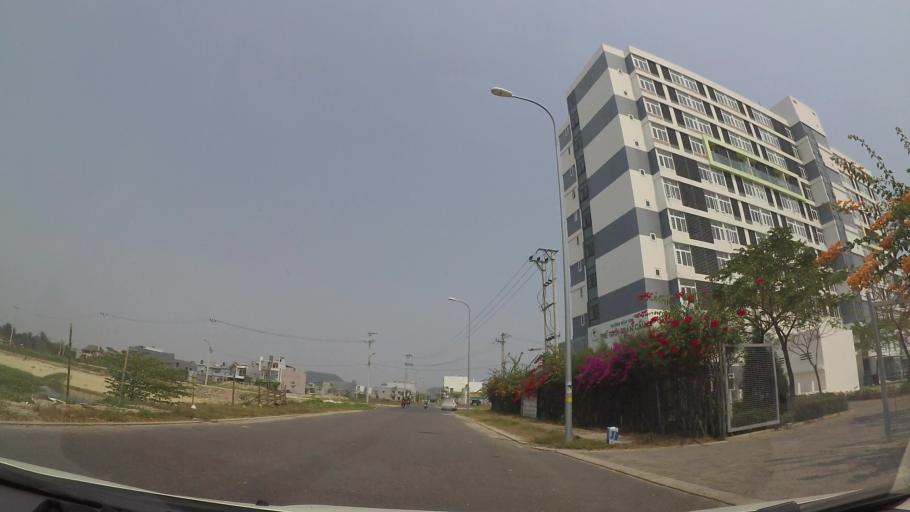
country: VN
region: Da Nang
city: Ngu Hanh Son
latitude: 15.9836
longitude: 108.2609
